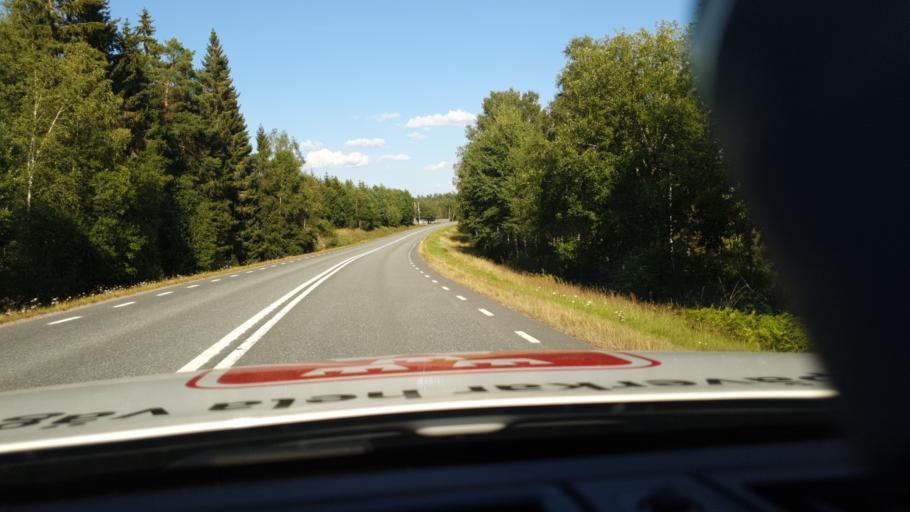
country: SE
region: Joenkoeping
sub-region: Eksjo Kommun
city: Eksjoe
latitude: 57.6927
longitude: 14.9613
